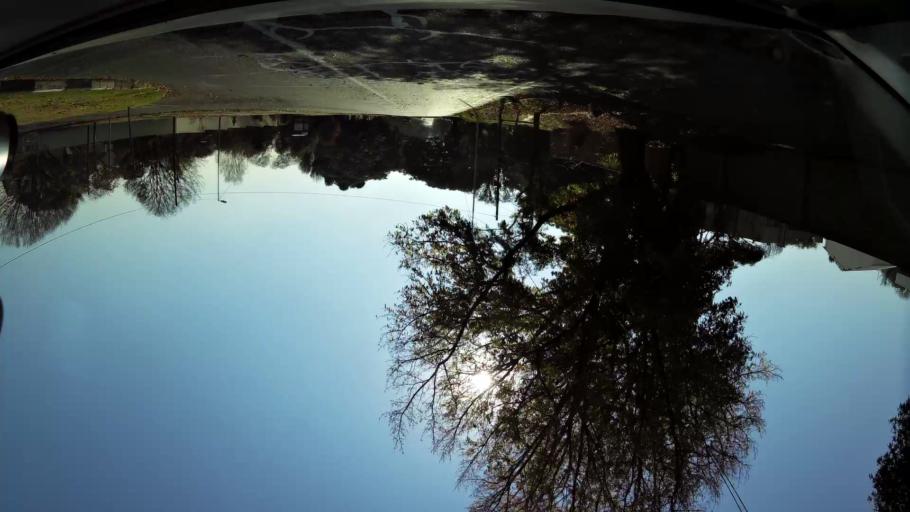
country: ZA
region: Gauteng
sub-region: City of Johannesburg Metropolitan Municipality
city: Modderfontein
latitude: -26.1422
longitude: 28.1118
